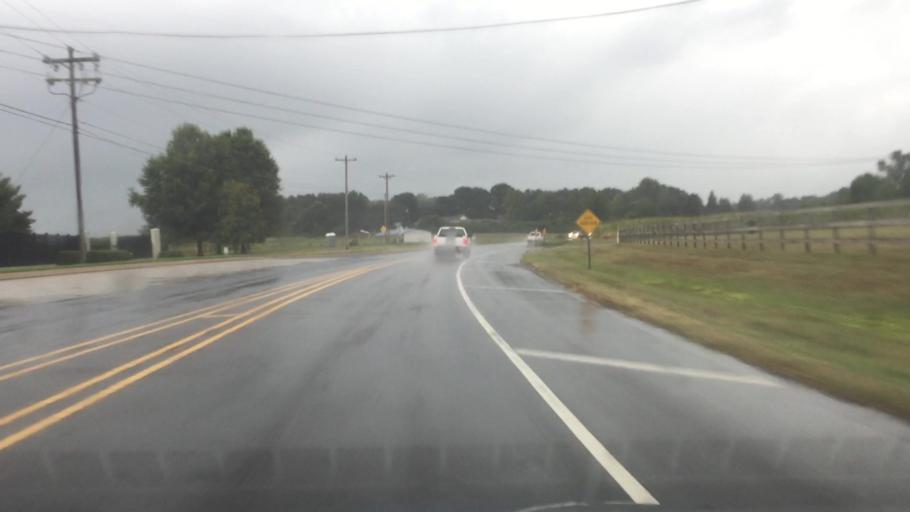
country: US
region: North Carolina
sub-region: Iredell County
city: Mooresville
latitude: 35.5417
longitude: -80.7684
